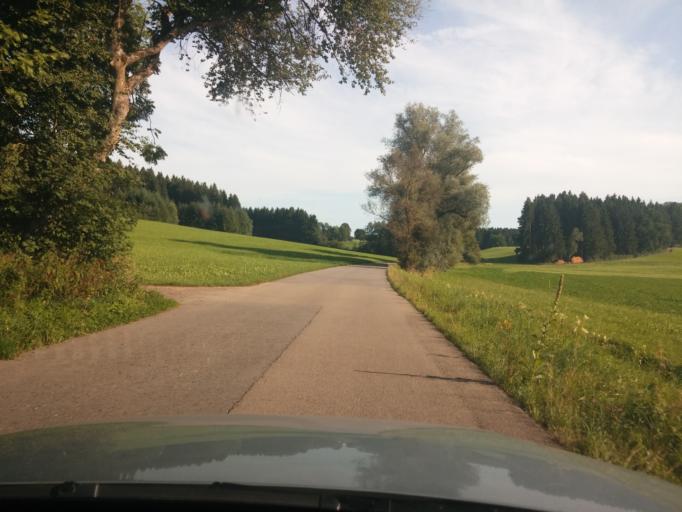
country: DE
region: Bavaria
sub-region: Swabia
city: Legau
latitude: 47.8561
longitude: 10.1056
